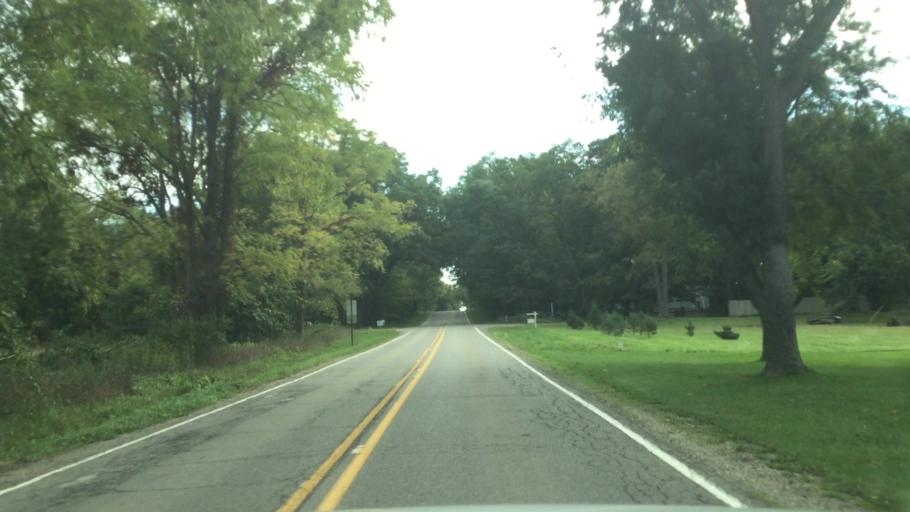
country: US
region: Michigan
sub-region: Genesee County
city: Argentine
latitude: 42.7044
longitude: -83.8614
